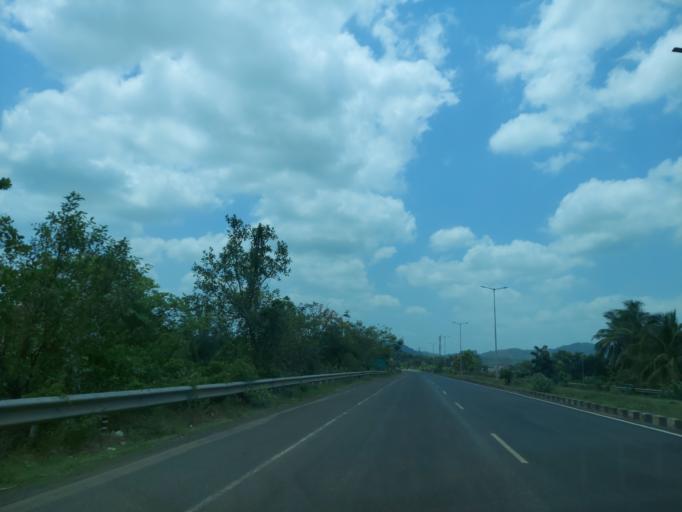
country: IN
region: Maharashtra
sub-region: Sindhudurg
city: Savantvadi
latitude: 15.8223
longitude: 73.8580
